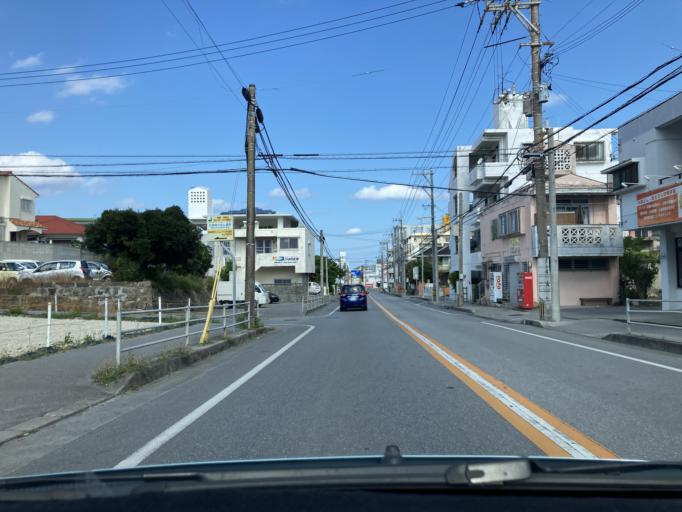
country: JP
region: Okinawa
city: Tomigusuku
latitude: 26.1855
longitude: 127.6812
